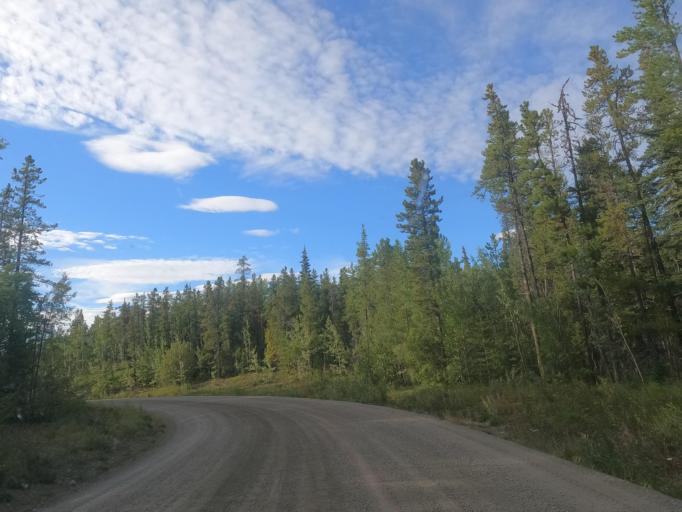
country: CA
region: Yukon
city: Whitehorse
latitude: 60.7542
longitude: -135.0347
